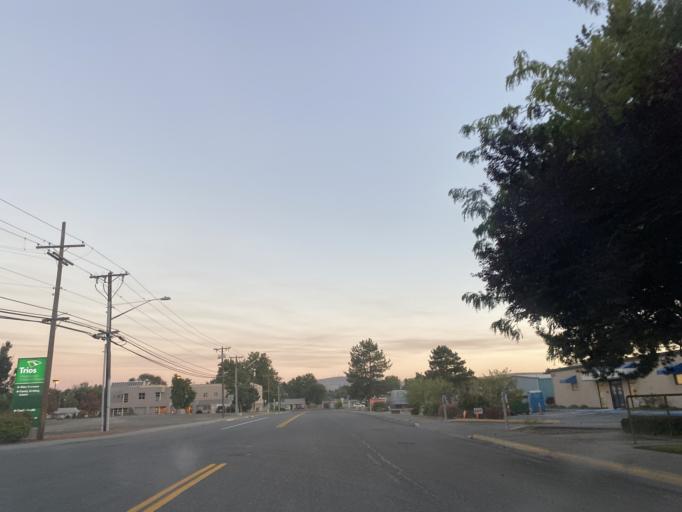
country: US
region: Washington
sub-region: Benton County
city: Kennewick
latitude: 46.2003
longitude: -119.1230
